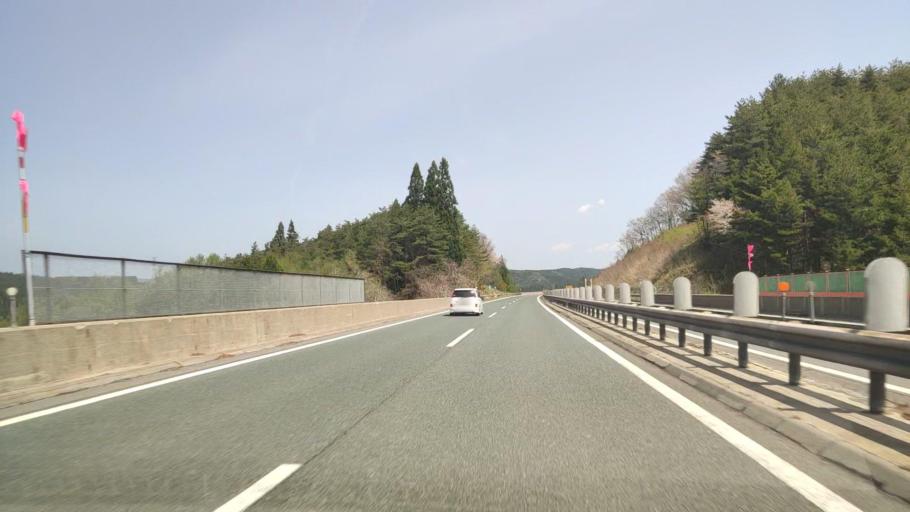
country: JP
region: Iwate
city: Ichinohe
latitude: 40.1536
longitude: 141.1193
